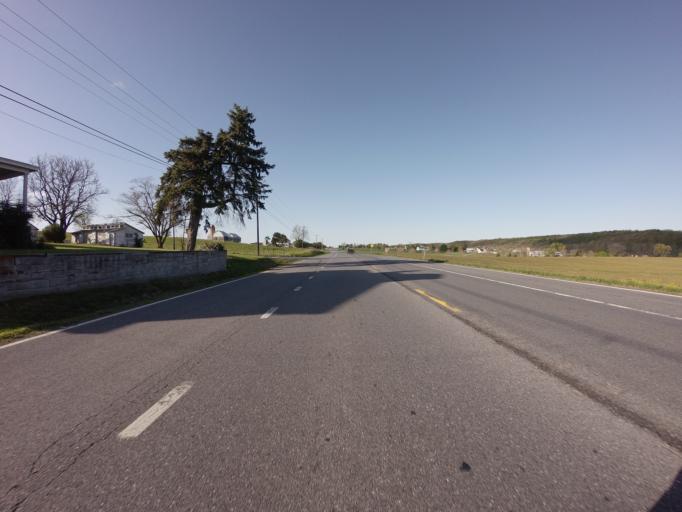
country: US
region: Maryland
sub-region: Frederick County
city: Woodsboro
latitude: 39.5135
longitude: -77.3196
